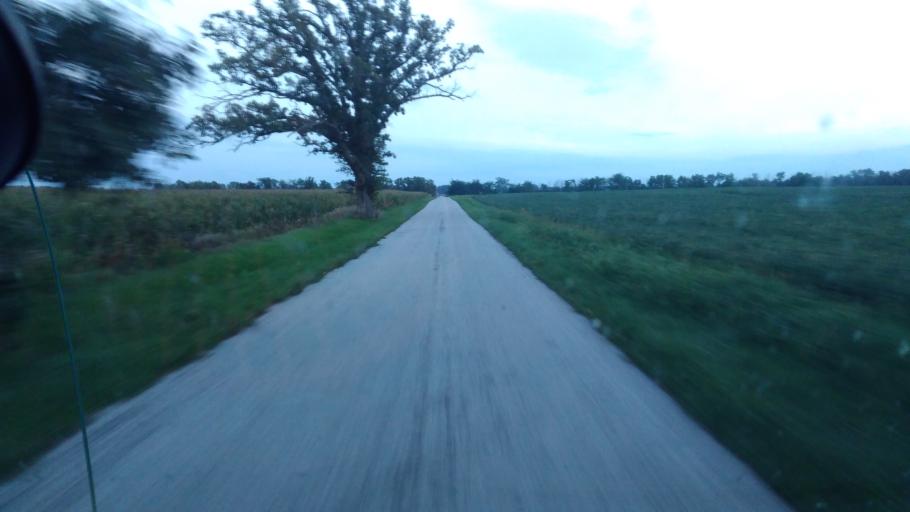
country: US
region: Ohio
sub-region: Hardin County
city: Forest
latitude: 40.6702
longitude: -83.4596
